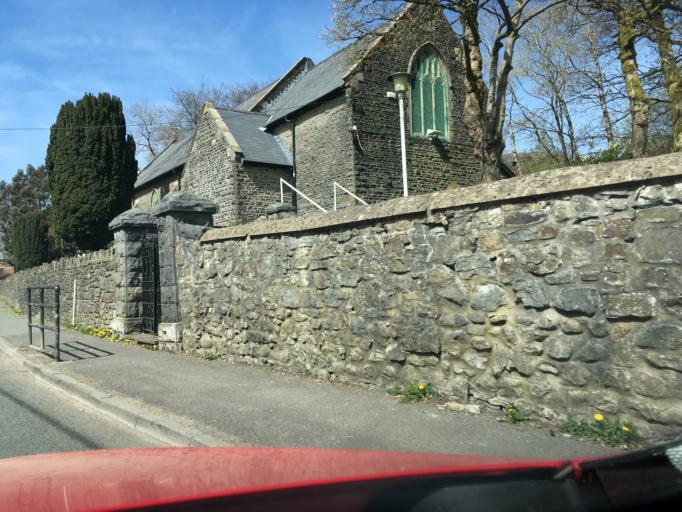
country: GB
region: Wales
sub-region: Merthyr Tydfil County Borough
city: Merthyr Tydfil
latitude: 51.7728
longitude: -3.3582
